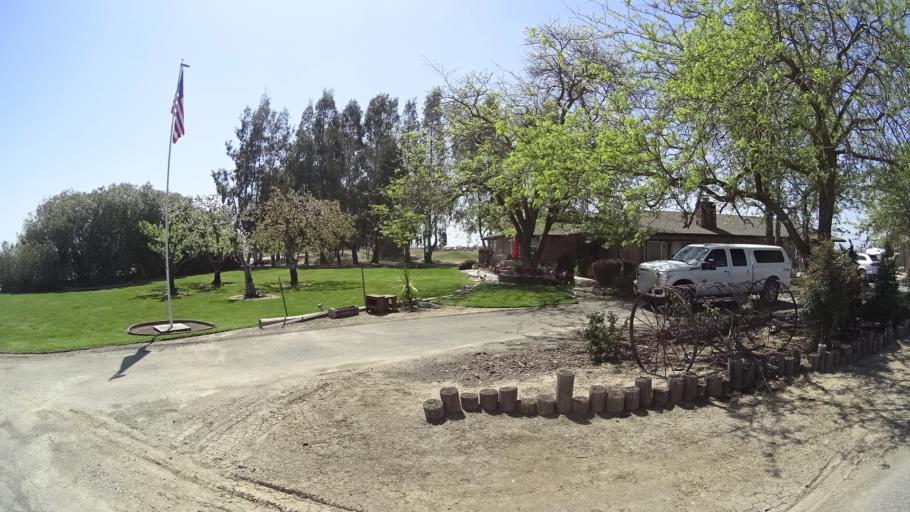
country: US
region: California
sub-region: Glenn County
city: Willows
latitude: 39.5437
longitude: -122.0889
